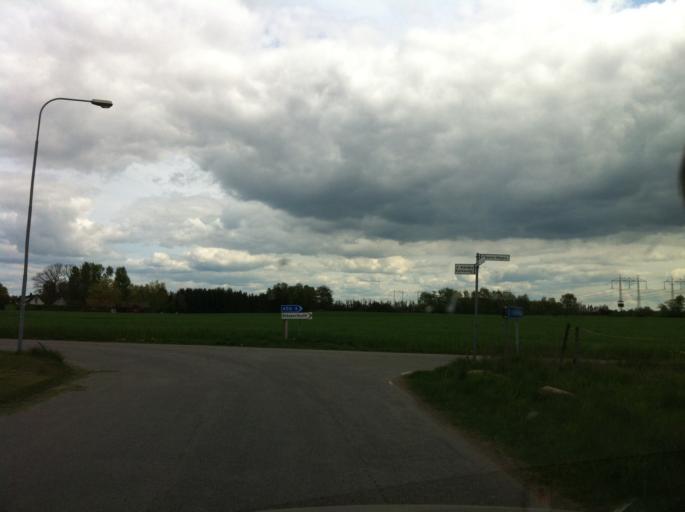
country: SE
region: Skane
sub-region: Kavlinge Kommun
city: Loddekopinge
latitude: 55.8042
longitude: 13.0389
